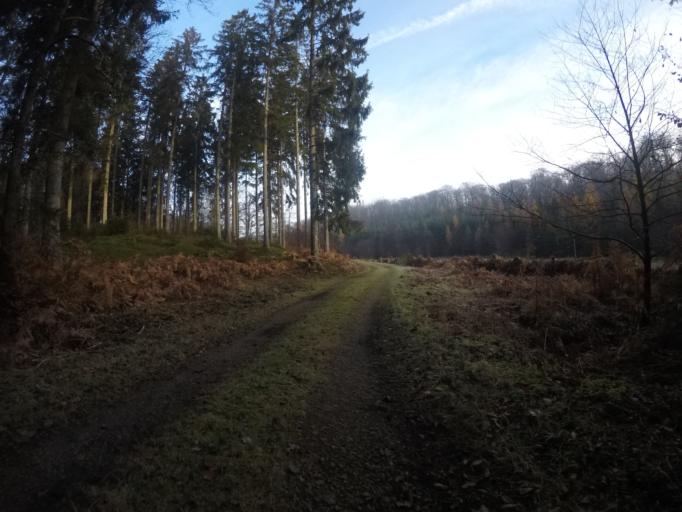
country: BE
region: Wallonia
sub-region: Province du Luxembourg
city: Habay-la-Vieille
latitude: 49.7591
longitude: 5.6599
